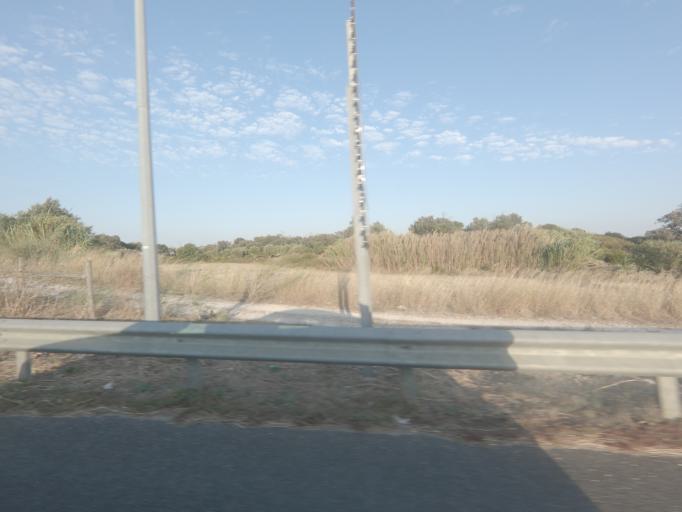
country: PT
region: Santarem
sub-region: Alcanena
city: Alcanena
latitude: 39.4773
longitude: -8.6362
